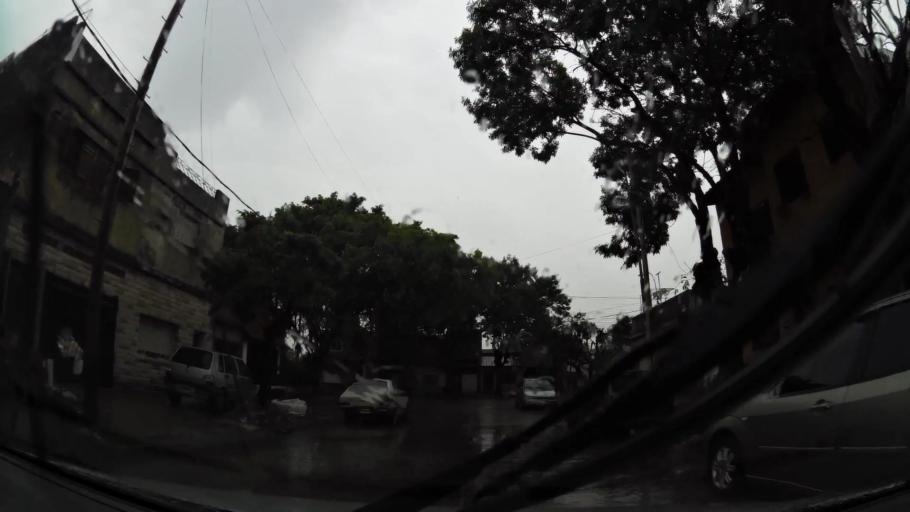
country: AR
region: Buenos Aires
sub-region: Partido de Lanus
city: Lanus
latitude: -34.7086
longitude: -58.4122
